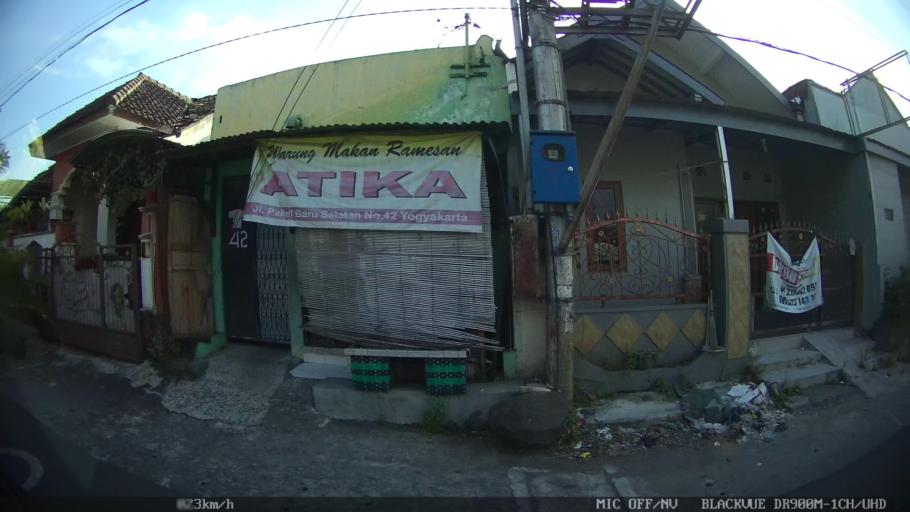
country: ID
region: Daerah Istimewa Yogyakarta
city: Yogyakarta
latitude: -7.8217
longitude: 110.3795
